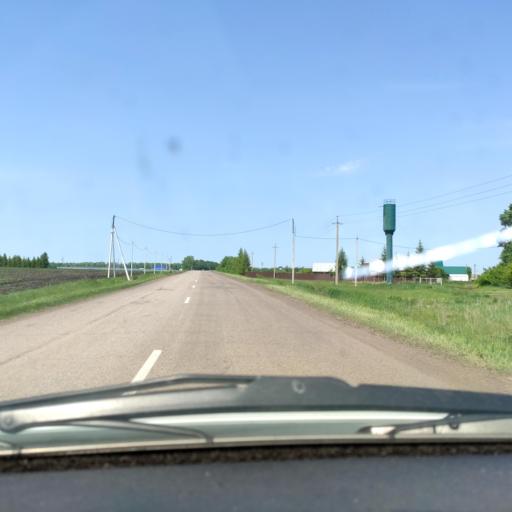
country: RU
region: Bashkortostan
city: Avdon
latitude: 54.4995
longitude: 55.6179
